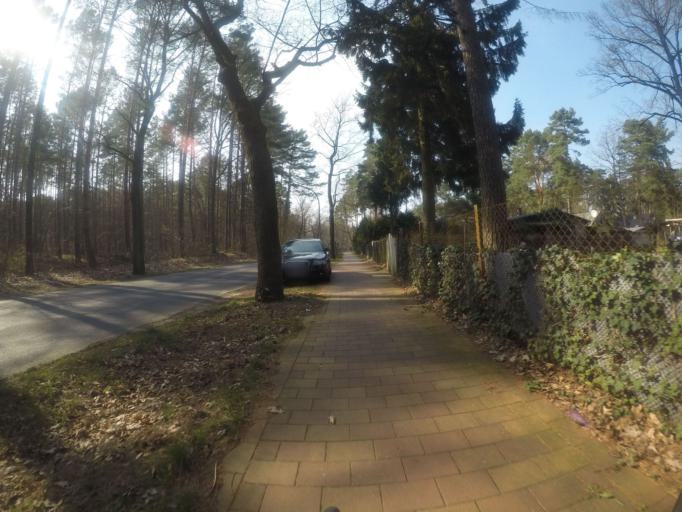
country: DE
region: Brandenburg
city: Bestensee
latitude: 52.2870
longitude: 13.6937
